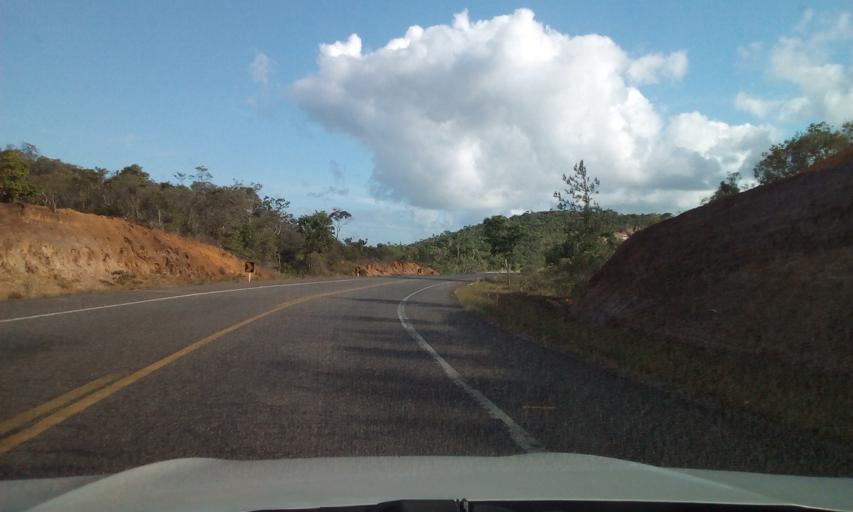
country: BR
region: Bahia
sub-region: Conde
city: Conde
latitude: -12.0905
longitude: -37.7737
